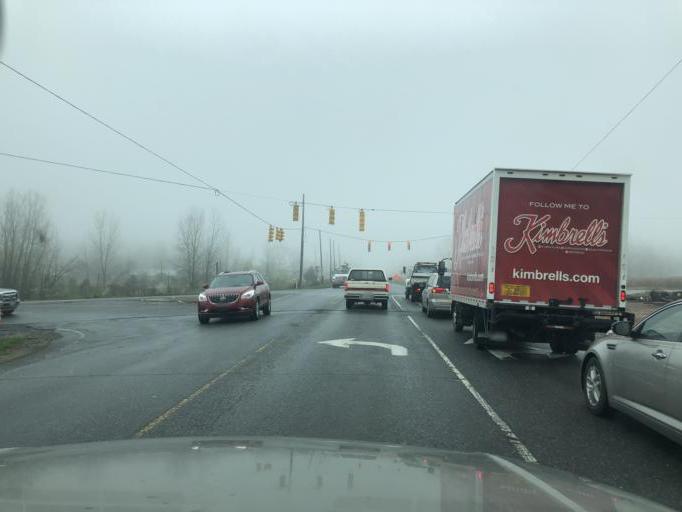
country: US
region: North Carolina
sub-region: Cleveland County
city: Shelby
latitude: 35.3134
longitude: -81.4905
